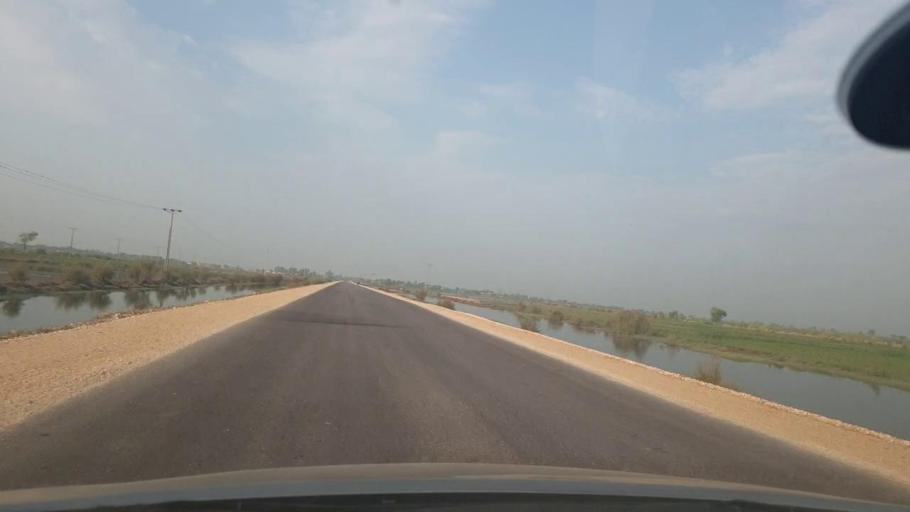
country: PK
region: Sindh
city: Jacobabad
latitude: 28.2250
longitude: 68.3780
